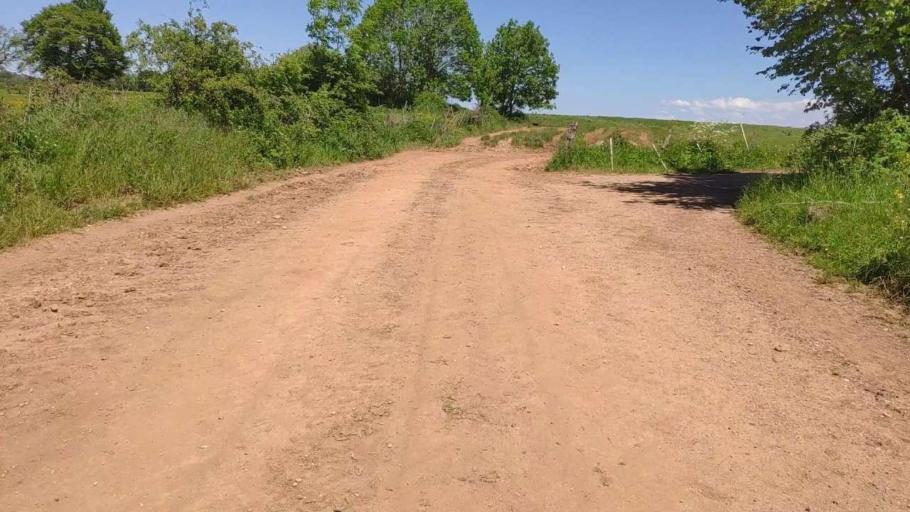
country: FR
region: Franche-Comte
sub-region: Departement du Jura
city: Poligny
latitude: 46.7684
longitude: 5.6878
